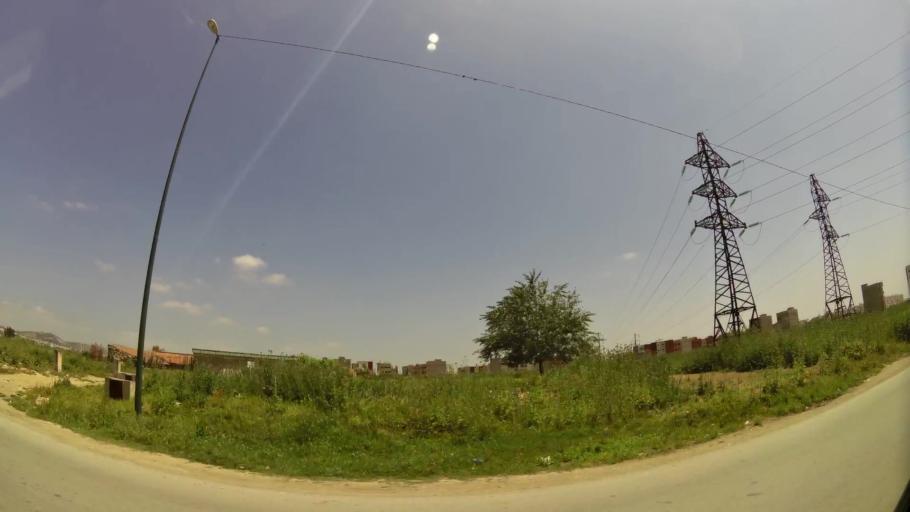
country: MA
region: Fes-Boulemane
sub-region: Fes
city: Fes
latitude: 34.0369
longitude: -5.0606
